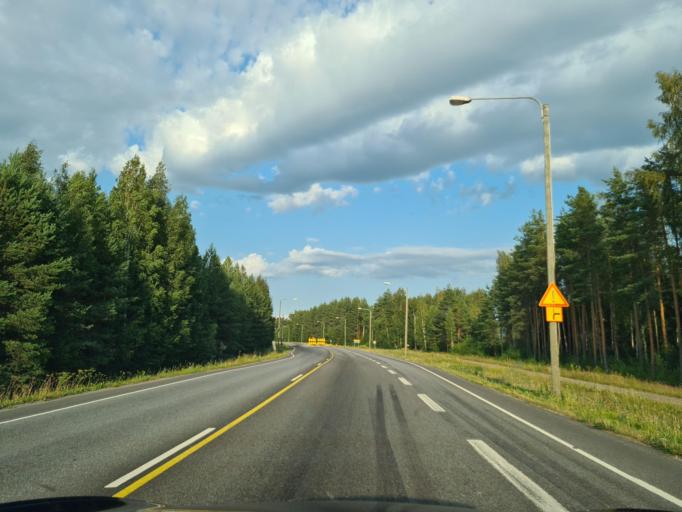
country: FI
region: Southern Ostrobothnia
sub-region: Seinaejoki
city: Lapua
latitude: 62.9866
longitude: 22.9363
